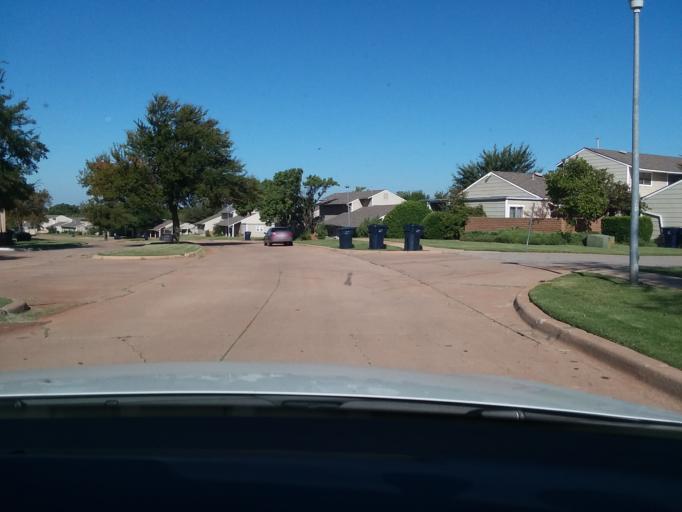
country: US
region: Oklahoma
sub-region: Oklahoma County
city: The Village
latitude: 35.5981
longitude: -97.5621
